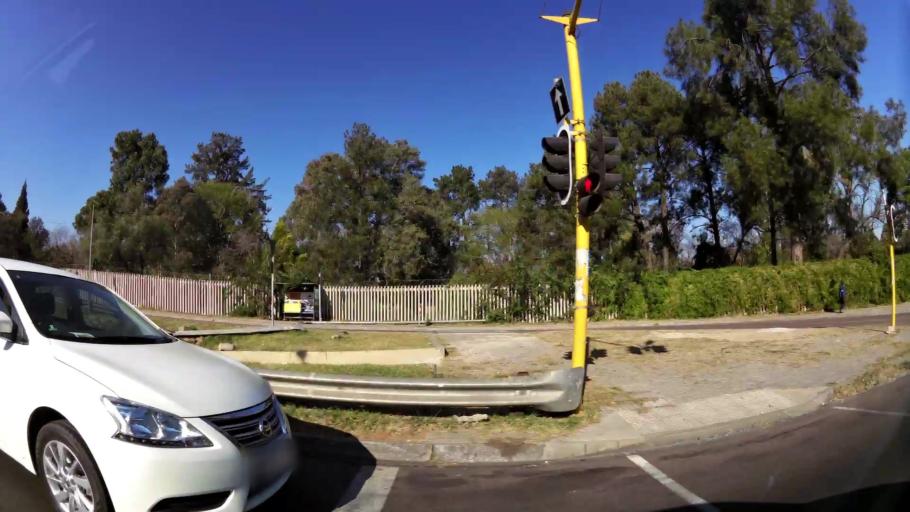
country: ZA
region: Gauteng
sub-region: City of Tshwane Metropolitan Municipality
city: Pretoria
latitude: -25.7337
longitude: 28.1879
